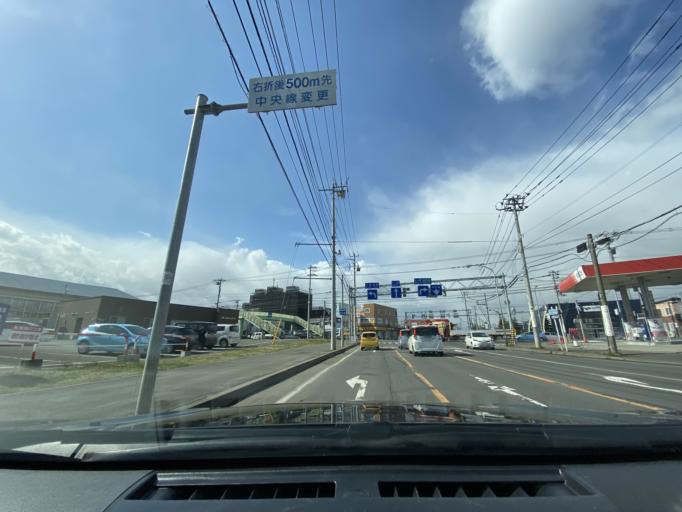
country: JP
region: Hokkaido
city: Kitahiroshima
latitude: 42.9723
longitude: 141.4776
